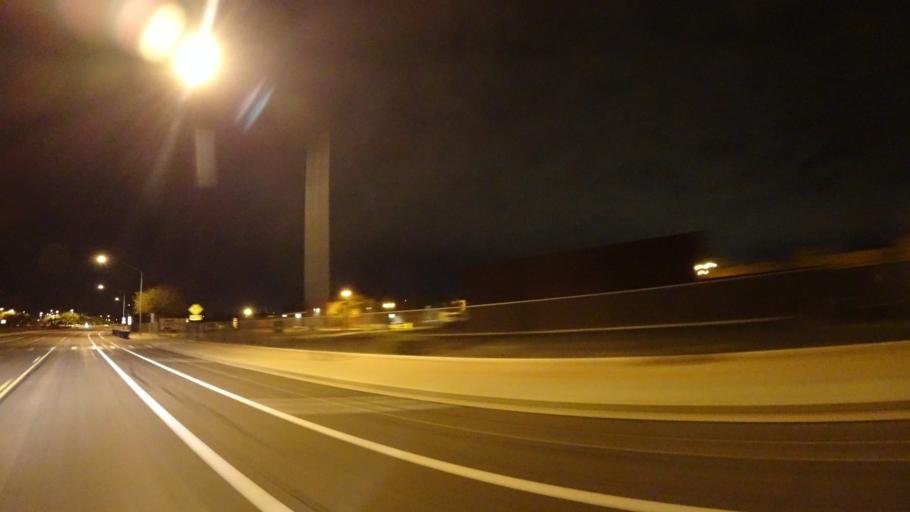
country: US
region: Arizona
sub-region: Pinal County
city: Apache Junction
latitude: 33.4344
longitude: -111.6719
